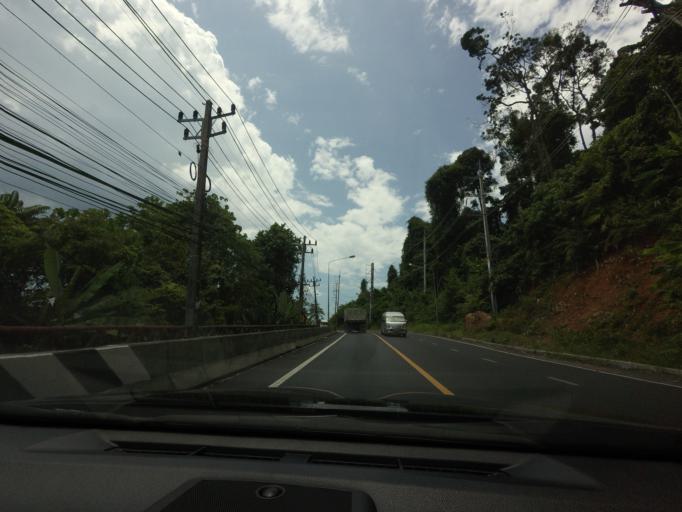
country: TH
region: Phangnga
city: Ban Khao Lak
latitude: 8.6336
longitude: 98.2461
